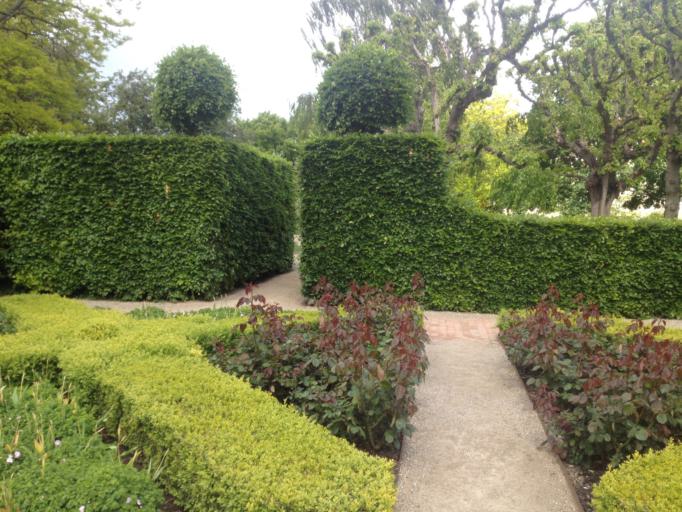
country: DK
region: Capital Region
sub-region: Kobenhavn
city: Copenhagen
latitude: 55.6862
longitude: 12.5780
